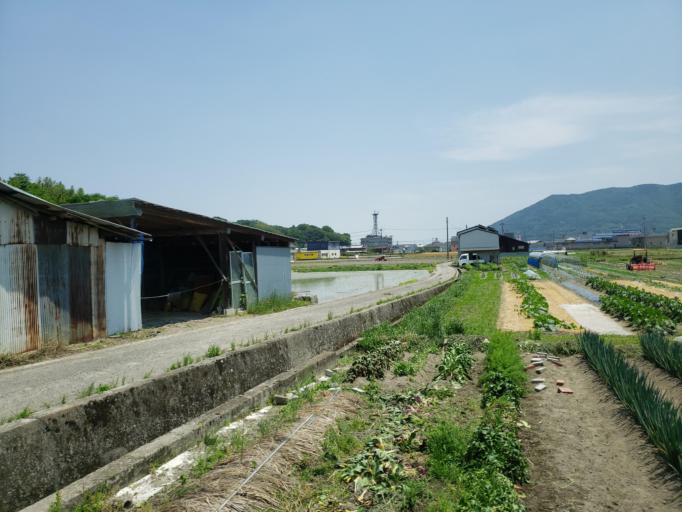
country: JP
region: Tokushima
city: Wakimachi
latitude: 34.0665
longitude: 134.1549
